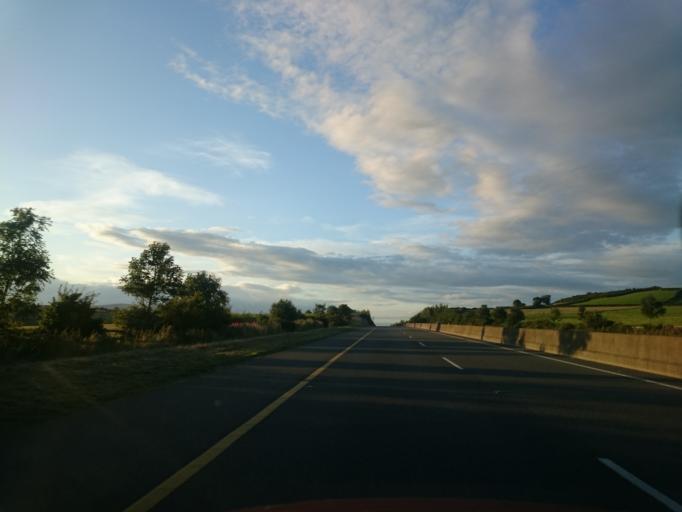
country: IE
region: Leinster
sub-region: Loch Garman
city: Gorey
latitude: 52.6925
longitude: -6.2639
